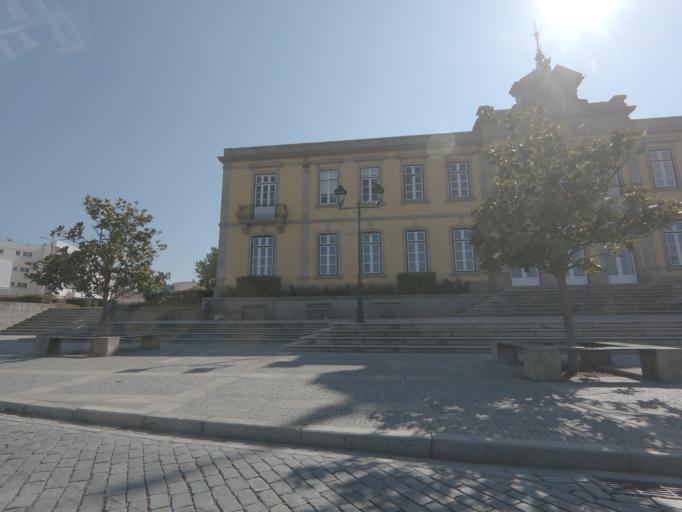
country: PT
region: Viseu
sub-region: Moimenta da Beira
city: Moimenta da Beira
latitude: 40.9799
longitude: -7.6133
